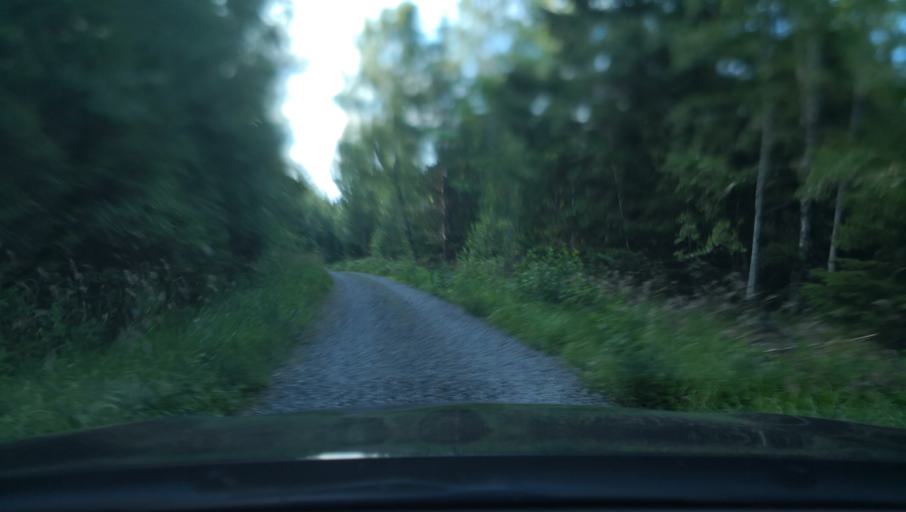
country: SE
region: Uppsala
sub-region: Osthammars Kommun
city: Osterbybruk
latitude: 60.0247
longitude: 17.9194
